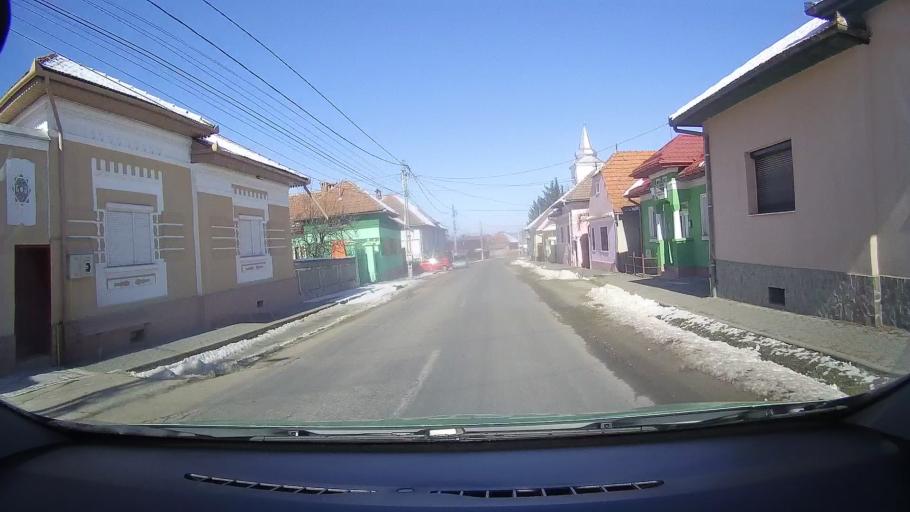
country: RO
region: Brasov
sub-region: Oras Victoria
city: Victoria
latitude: 45.7459
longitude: 24.7399
